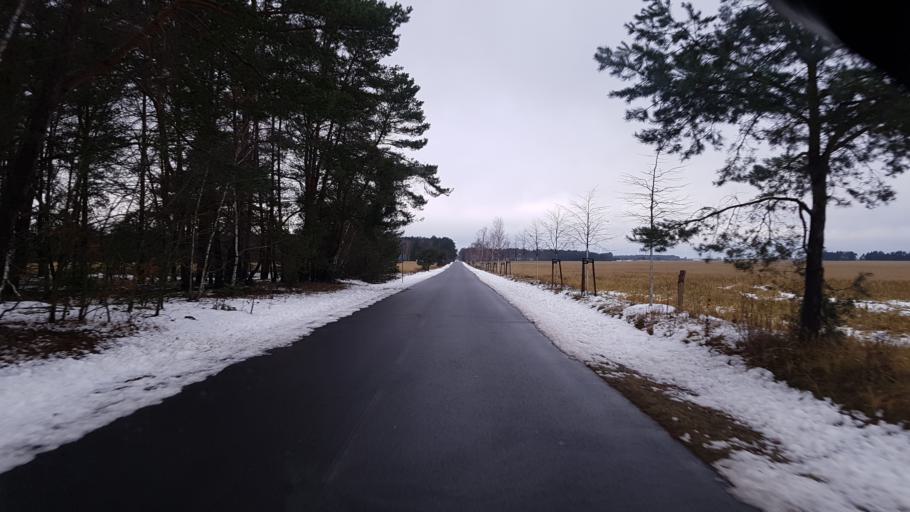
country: DE
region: Brandenburg
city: Luckau
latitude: 51.8662
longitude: 13.8110
